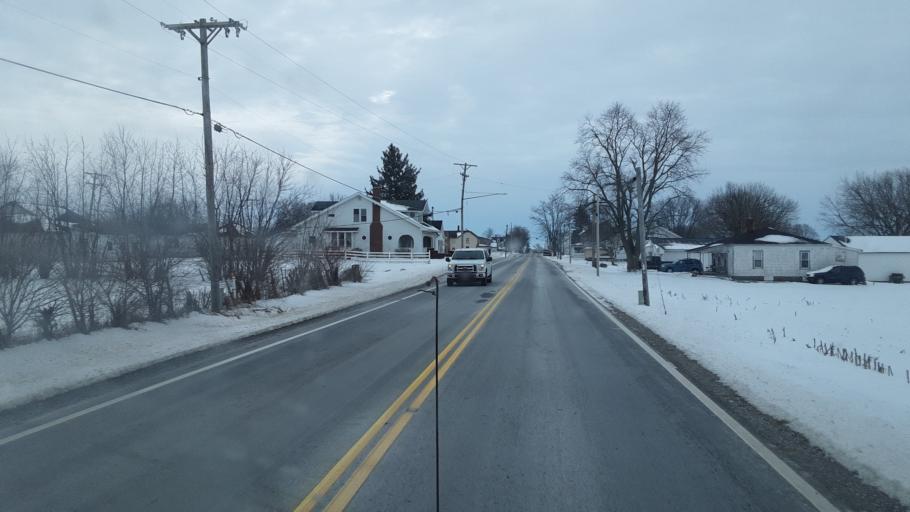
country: US
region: Ohio
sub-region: Madison County
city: Bethel
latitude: 39.7361
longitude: -83.4768
